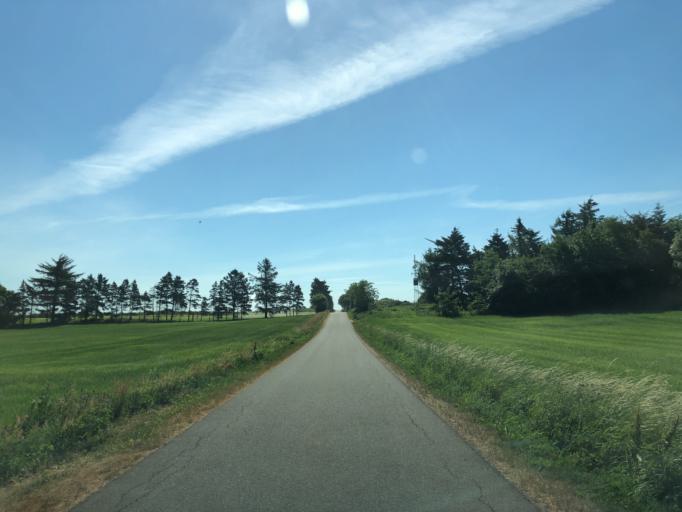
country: DK
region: Central Jutland
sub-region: Struer Kommune
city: Struer
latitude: 56.4303
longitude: 8.4587
